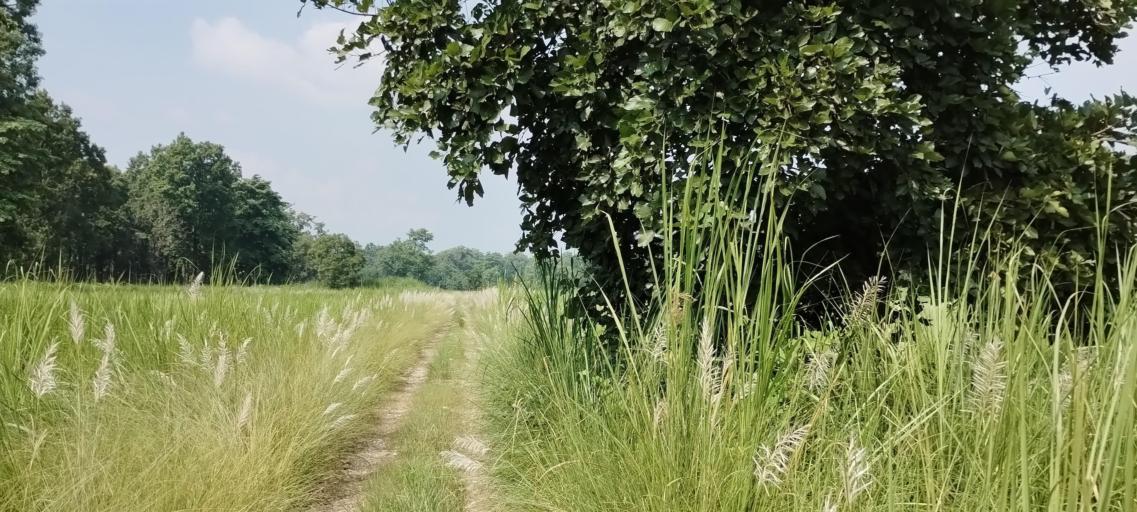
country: NP
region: Far Western
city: Tikapur
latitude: 28.5096
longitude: 81.2519
